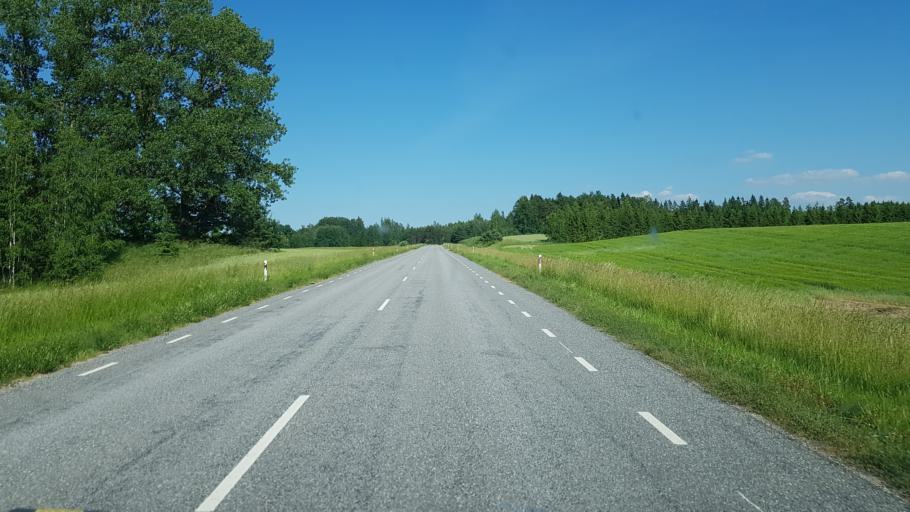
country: EE
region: Vorumaa
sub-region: Voru linn
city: Voru
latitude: 57.8579
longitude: 27.2243
